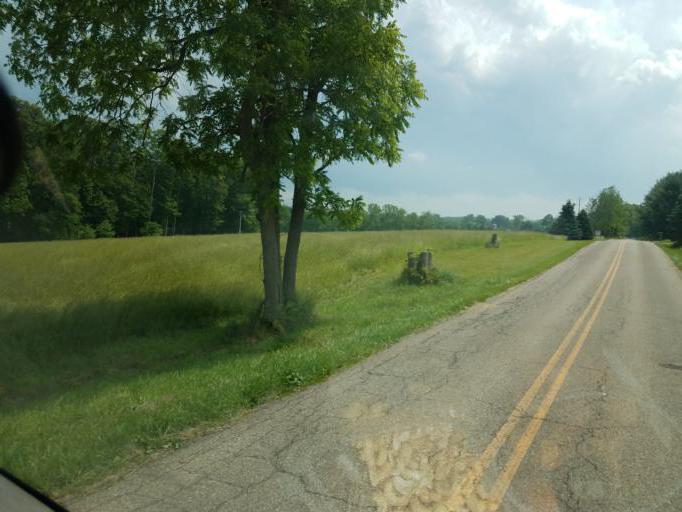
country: US
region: Ohio
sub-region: Knox County
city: Oak Hill
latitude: 40.3607
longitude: -82.2753
